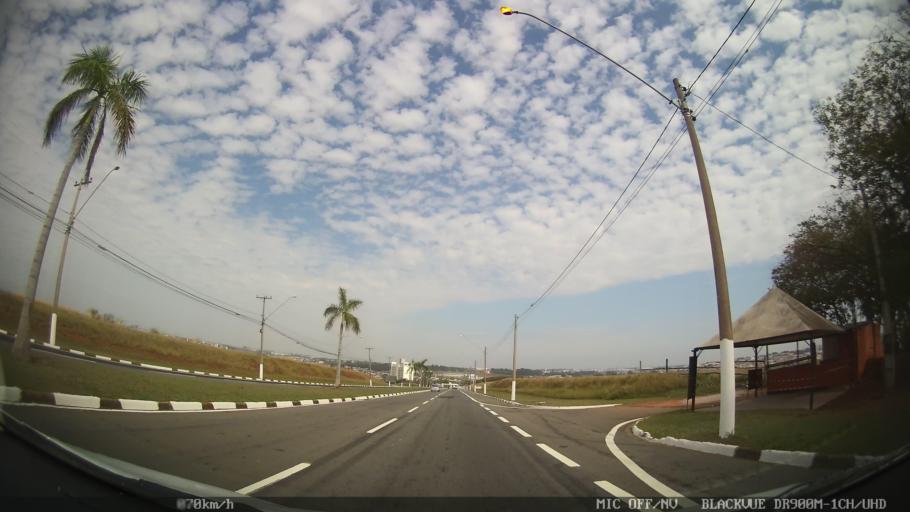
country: BR
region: Sao Paulo
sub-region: Paulinia
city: Paulinia
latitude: -22.7961
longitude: -47.1735
